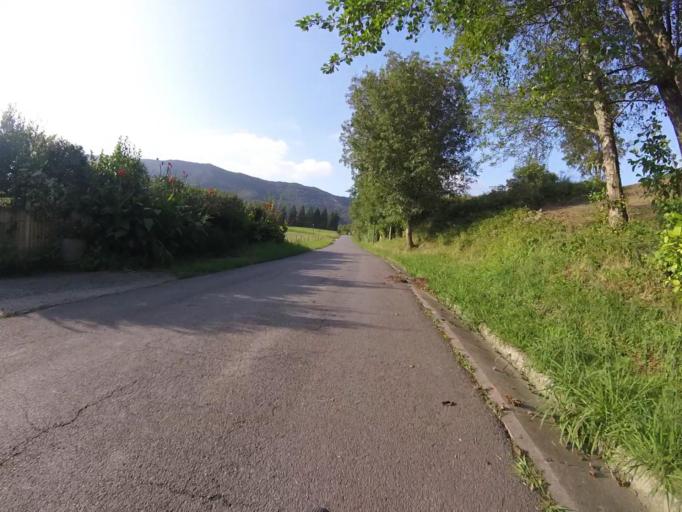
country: ES
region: Basque Country
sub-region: Provincia de Guipuzcoa
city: Irun
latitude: 43.3371
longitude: -1.8339
